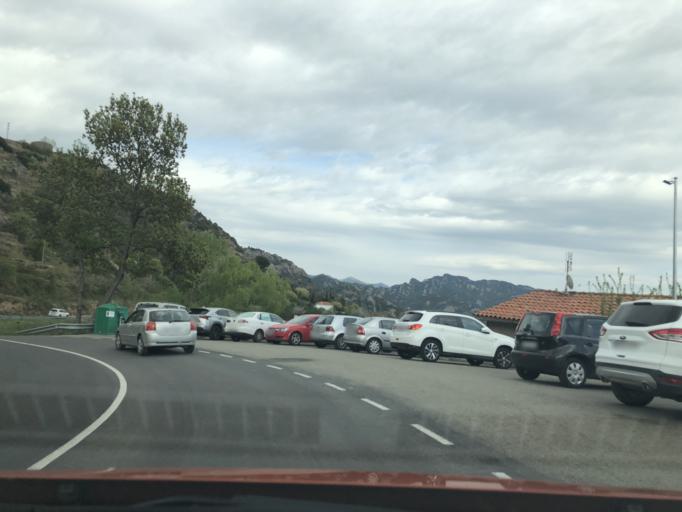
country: ES
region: Catalonia
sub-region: Provincia de Barcelona
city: Berga
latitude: 42.1074
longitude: 1.8519
